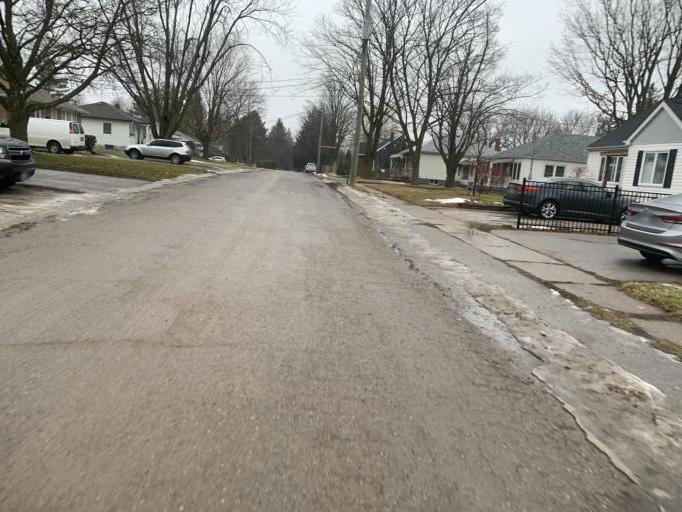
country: CA
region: Ontario
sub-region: Halton
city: Milton
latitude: 43.6557
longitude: -79.9326
